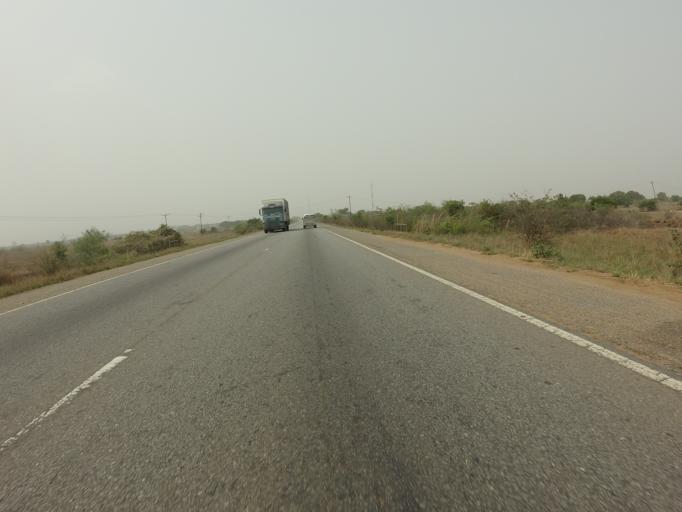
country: GH
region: Greater Accra
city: Tema
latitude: 5.8677
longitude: 0.3029
